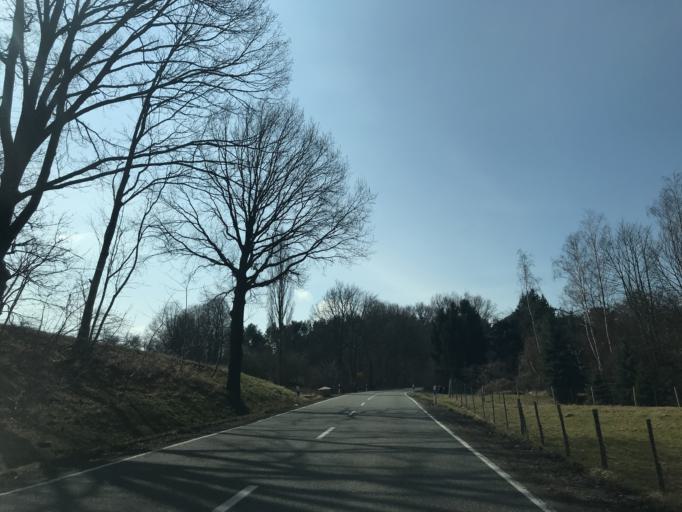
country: DE
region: Saxony
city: Rochlitz
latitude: 51.0420
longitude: 12.8053
